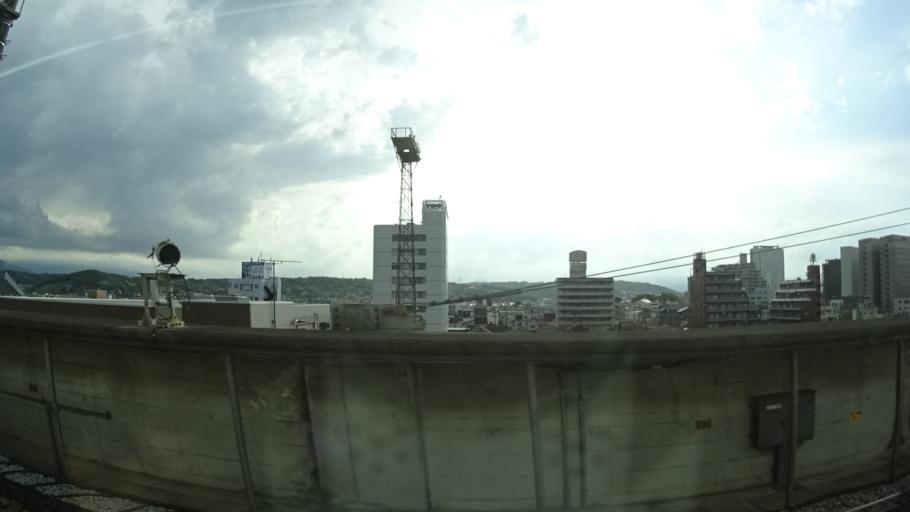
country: JP
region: Gunma
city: Takasaki
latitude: 36.3188
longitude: 139.0134
